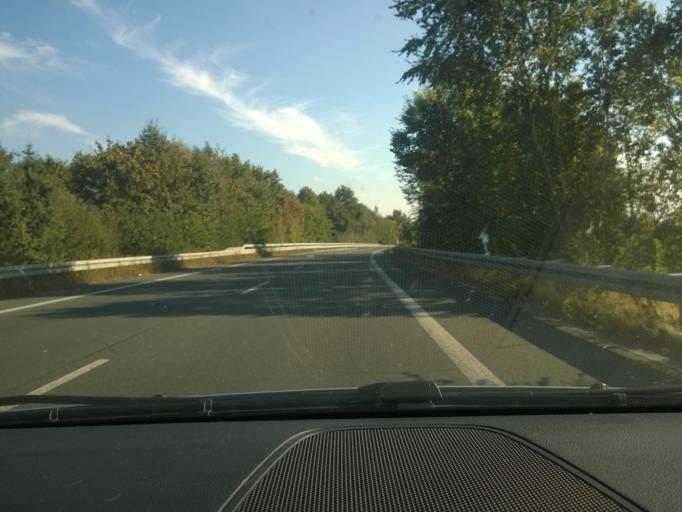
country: DE
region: North Rhine-Westphalia
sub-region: Regierungsbezirk Munster
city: Sudlohn
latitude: 51.9008
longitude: 6.8560
